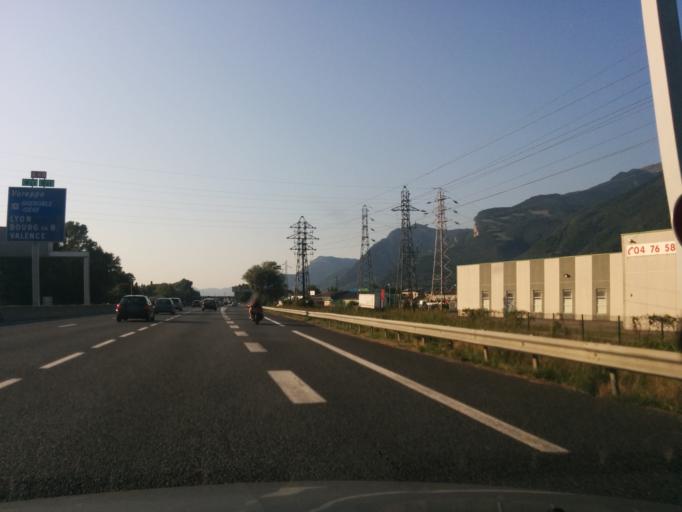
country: FR
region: Rhone-Alpes
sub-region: Departement de l'Isere
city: Fontanil-Cornillon
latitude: 45.2324
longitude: 5.6646
